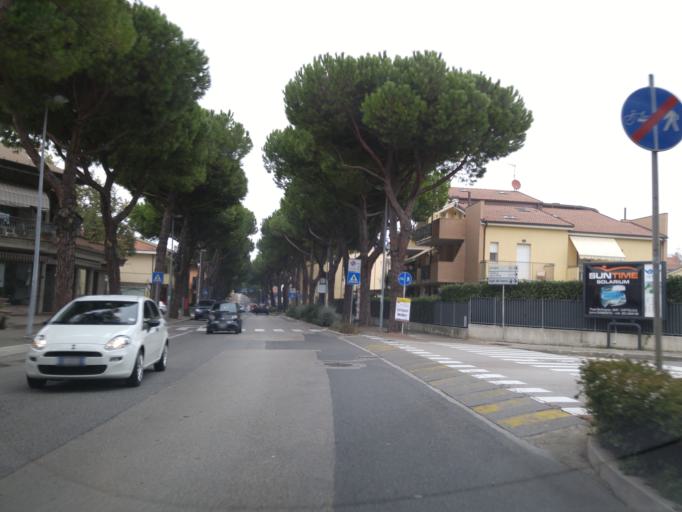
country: IT
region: Emilia-Romagna
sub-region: Provincia di Rimini
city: Cattolica
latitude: 43.9601
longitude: 12.7338
